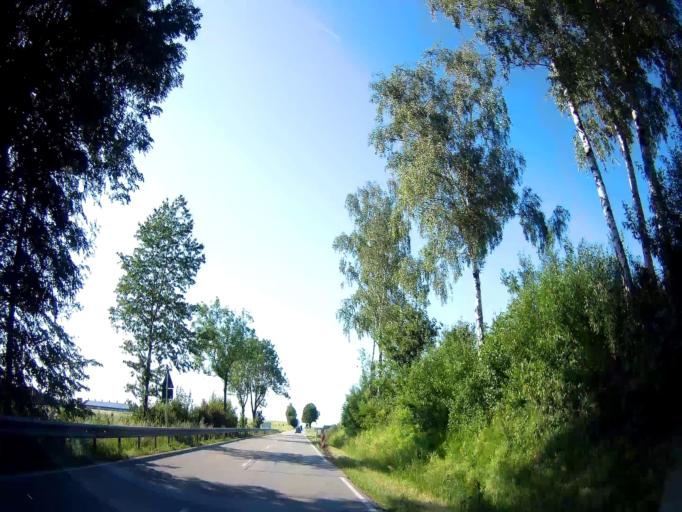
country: DE
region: Bavaria
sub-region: Lower Bavaria
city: Zeilarn
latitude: 48.3312
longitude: 12.8261
